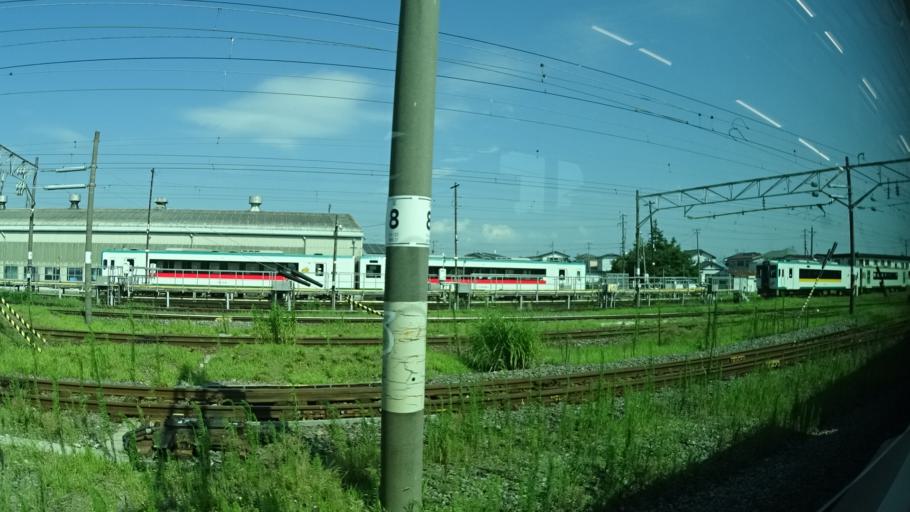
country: JP
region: Miyagi
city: Kogota
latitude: 38.5364
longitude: 141.0645
